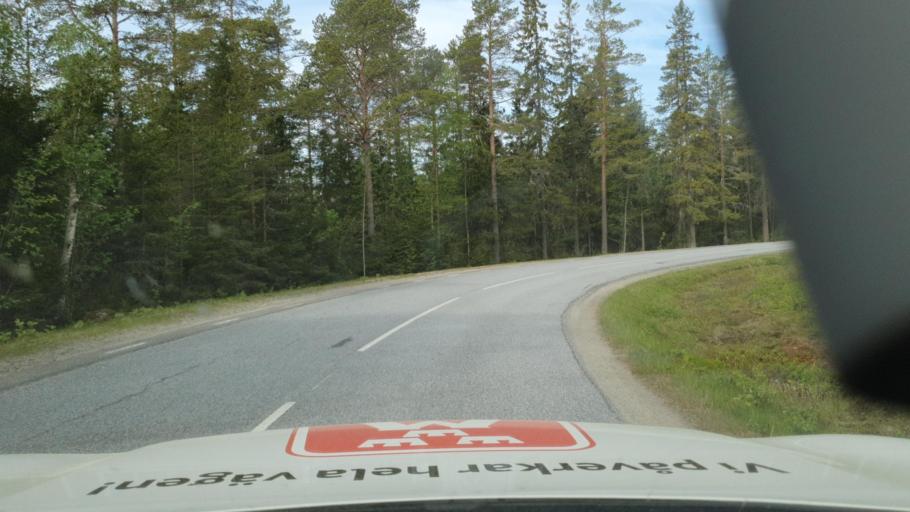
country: SE
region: Vaesterbotten
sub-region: Umea Kommun
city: Roback
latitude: 63.6764
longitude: 20.0847
